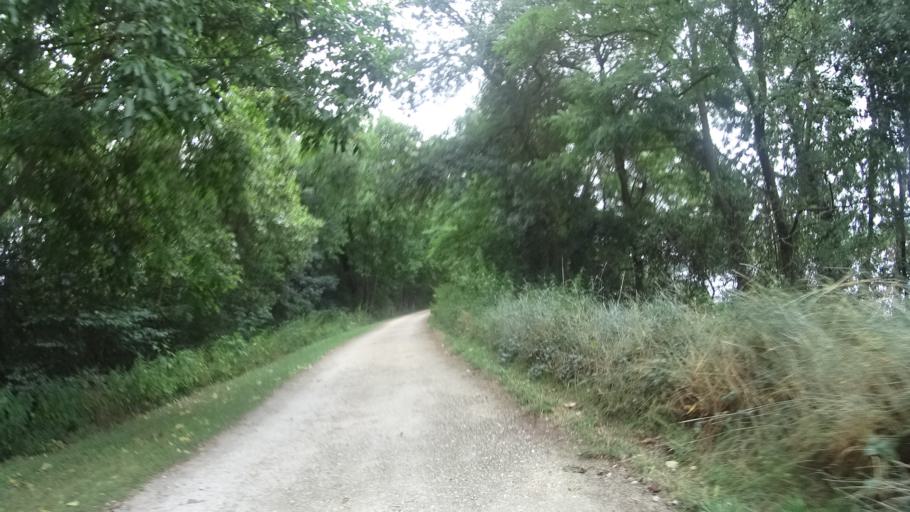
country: FR
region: Centre
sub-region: Departement du Loir-et-Cher
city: La Chaussee-Saint-Victor
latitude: 47.6215
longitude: 1.3895
